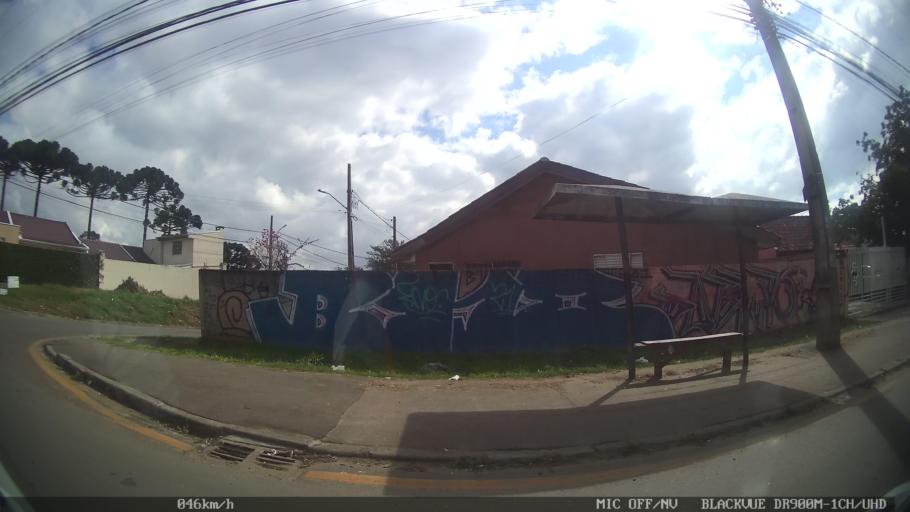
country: BR
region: Parana
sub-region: Colombo
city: Colombo
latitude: -25.3647
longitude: -49.2141
